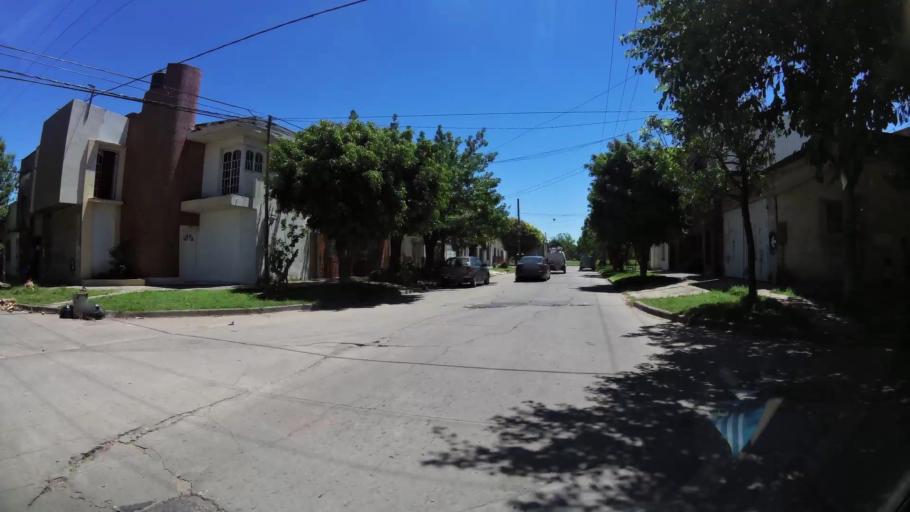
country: AR
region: Santa Fe
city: Santa Fe de la Vera Cruz
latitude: -31.6256
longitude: -60.7088
